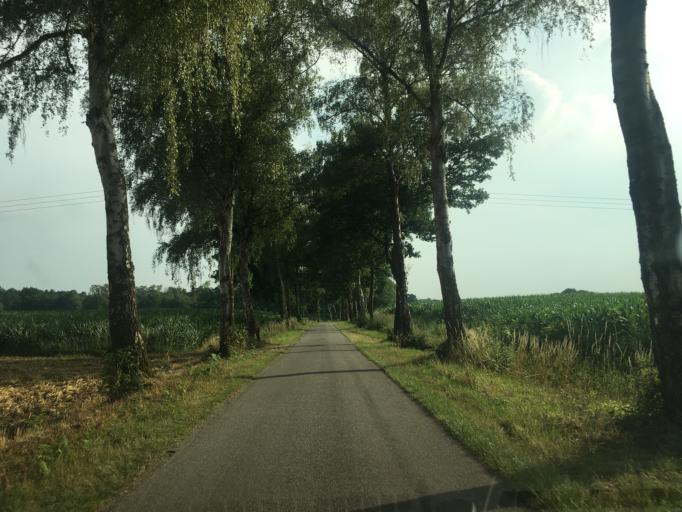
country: DE
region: North Rhine-Westphalia
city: Olfen
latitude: 51.7369
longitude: 7.3435
